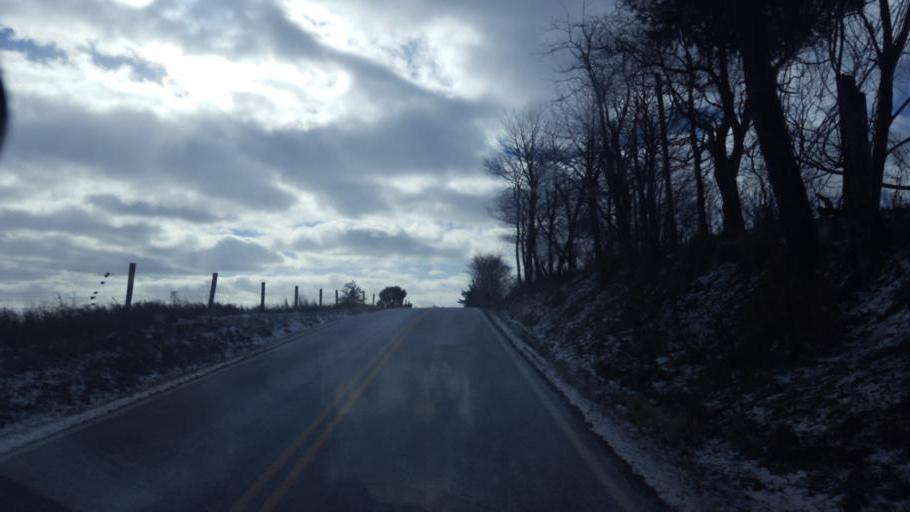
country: US
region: Ohio
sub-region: Coshocton County
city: West Lafayette
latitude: 40.3405
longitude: -81.7776
